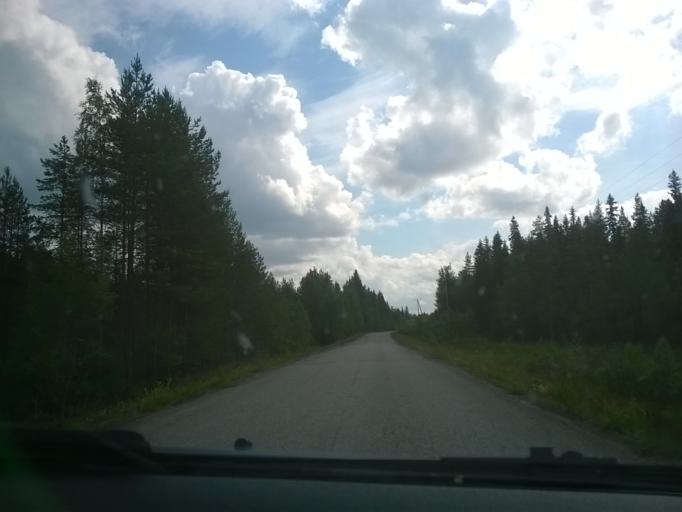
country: FI
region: Kainuu
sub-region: Kehys-Kainuu
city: Kuhmo
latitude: 64.4227
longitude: 29.7527
